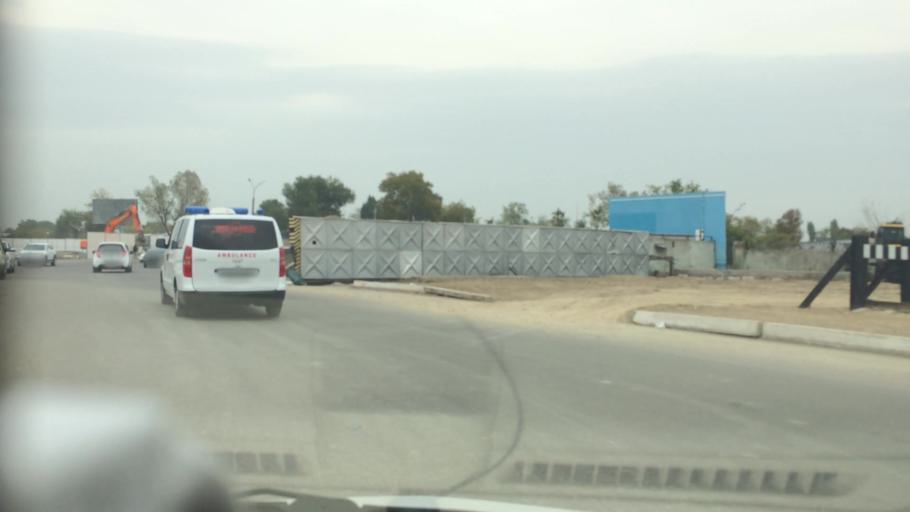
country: UZ
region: Toshkent
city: Salor
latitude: 41.3055
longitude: 69.3391
